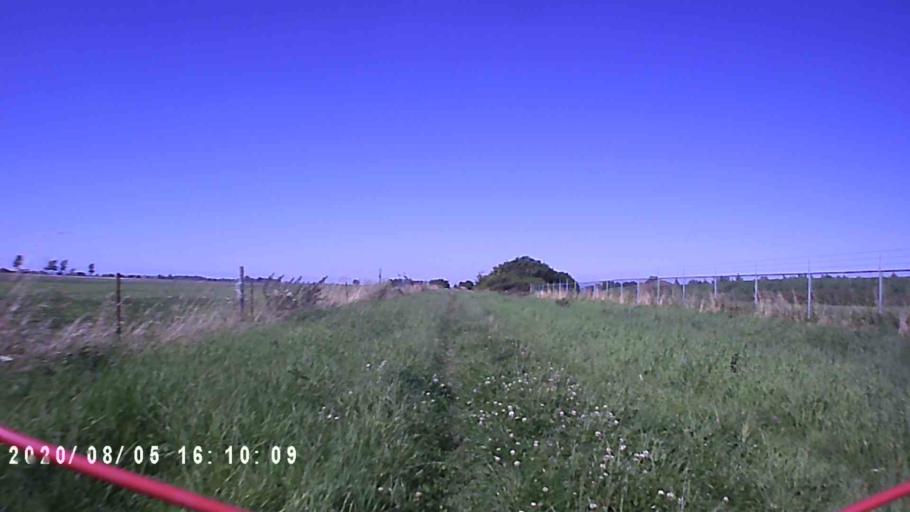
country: NL
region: Groningen
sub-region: Gemeente Winsum
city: Winsum
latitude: 53.3955
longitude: 6.5204
